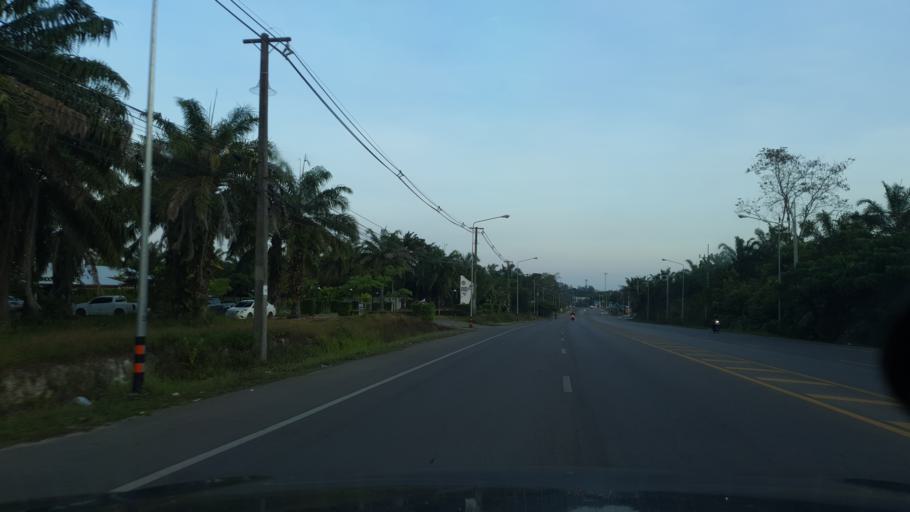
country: TH
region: Phangnga
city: Ban Ao Nang
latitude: 8.0378
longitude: 98.8540
